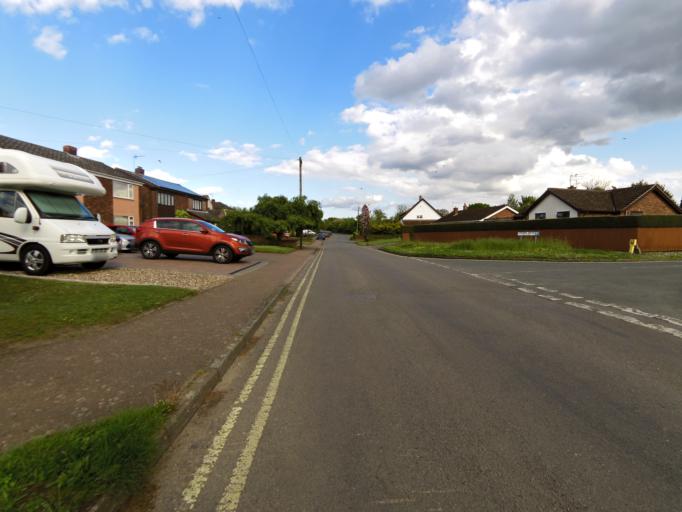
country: GB
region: England
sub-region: Suffolk
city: Stowmarket
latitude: 52.1969
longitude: 0.9589
